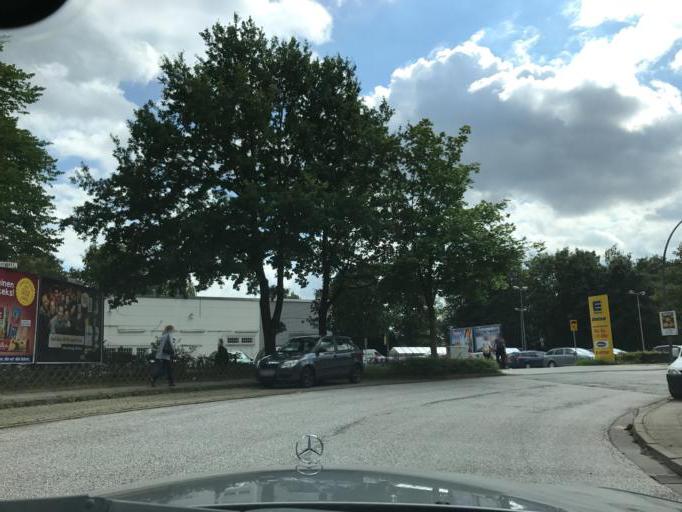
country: DE
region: Schleswig-Holstein
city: Glinde
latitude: 53.5144
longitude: 10.2113
